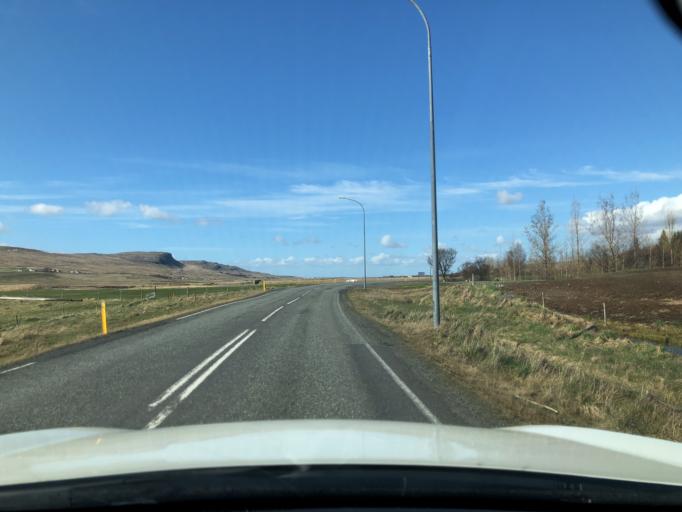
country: IS
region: Capital Region
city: Mosfellsbaer
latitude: 64.6626
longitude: -21.2876
